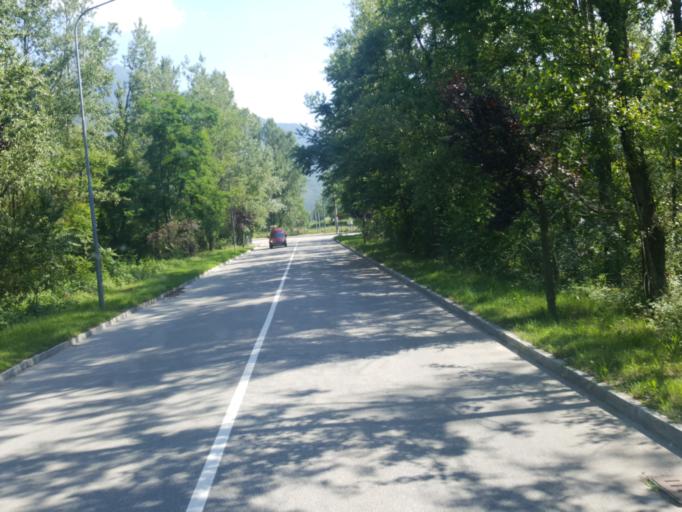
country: IT
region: Piedmont
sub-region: Provincia Verbano-Cusio-Ossola
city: Domodossola
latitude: 46.1004
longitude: 8.2997
